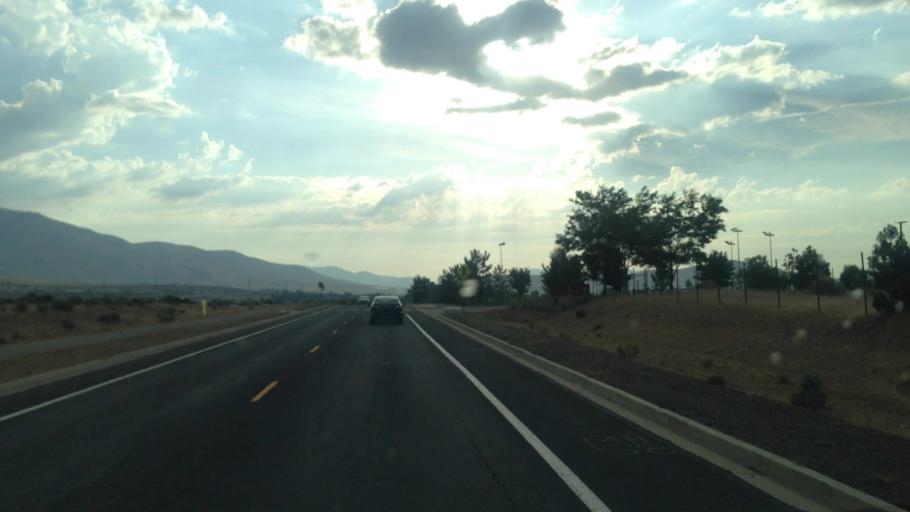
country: US
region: Nevada
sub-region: Washoe County
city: Lemmon Valley
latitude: 39.6214
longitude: -119.8634
